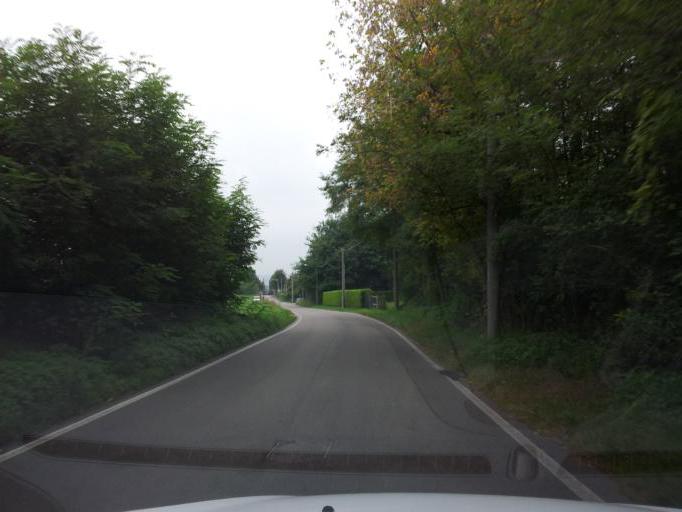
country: IT
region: Lombardy
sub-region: Provincia di Varese
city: Sesto Calende
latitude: 45.7309
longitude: 8.6469
